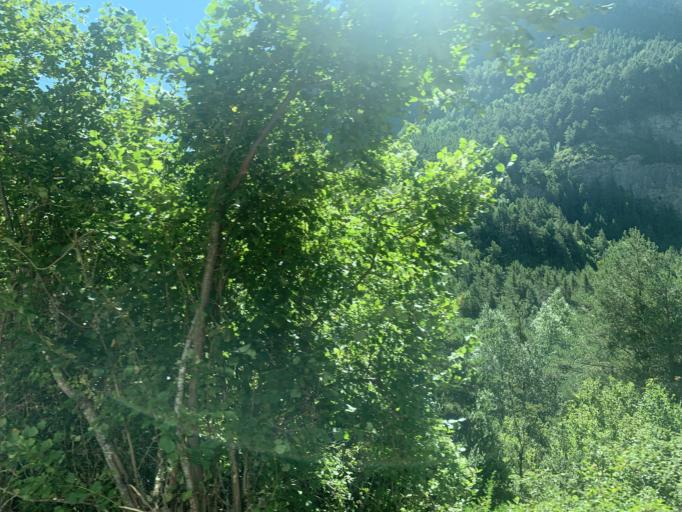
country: ES
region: Aragon
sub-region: Provincia de Huesca
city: Broto
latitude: 42.6511
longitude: -0.1052
